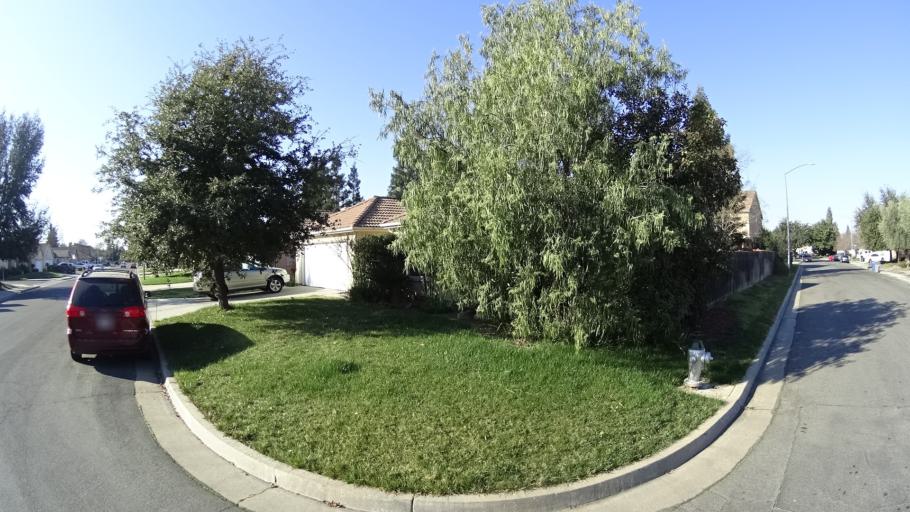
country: US
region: California
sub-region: Fresno County
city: Clovis
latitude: 36.8706
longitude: -119.7349
